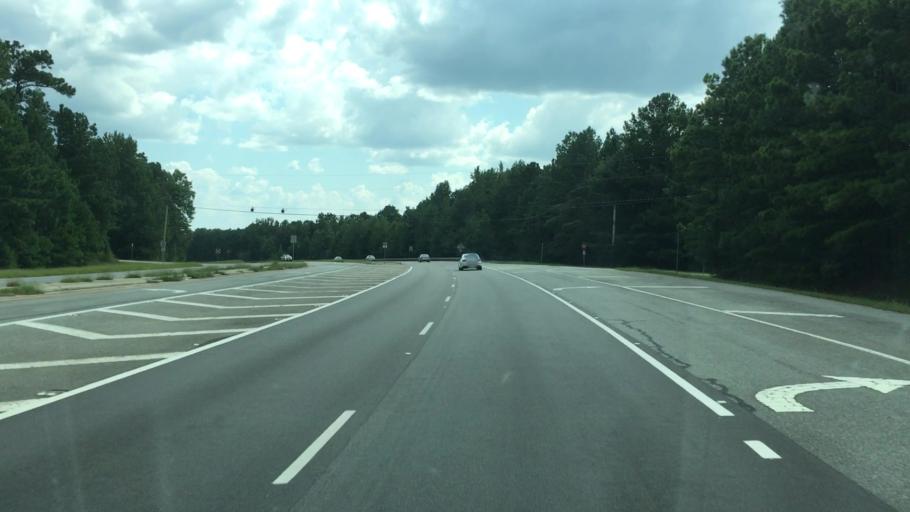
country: US
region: Georgia
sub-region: Putnam County
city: Eatonton
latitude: 33.3359
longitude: -83.4088
